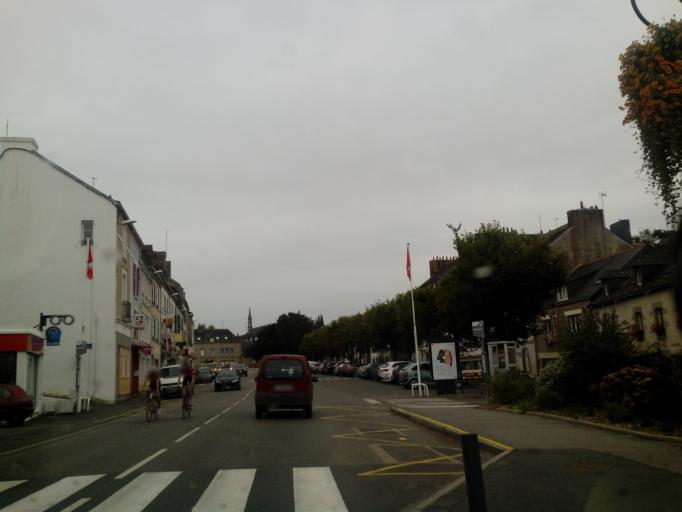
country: FR
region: Brittany
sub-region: Departement du Finistere
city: Quimperle
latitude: 47.8710
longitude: -3.5446
